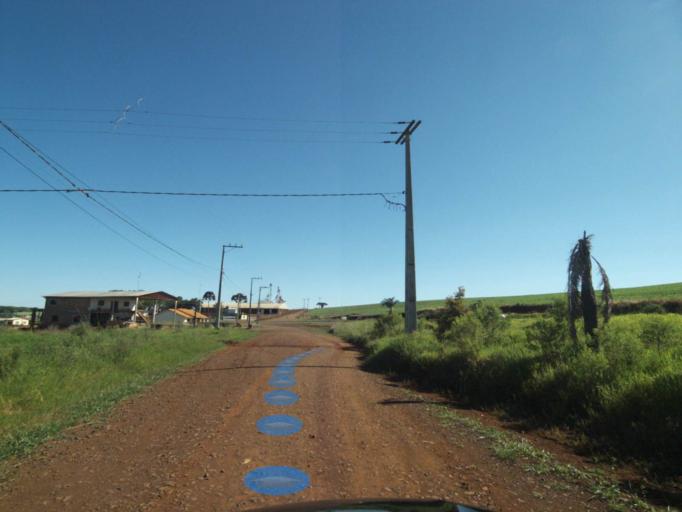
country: BR
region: Parana
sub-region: Coronel Vivida
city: Coronel Vivida
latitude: -26.1385
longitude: -52.3935
